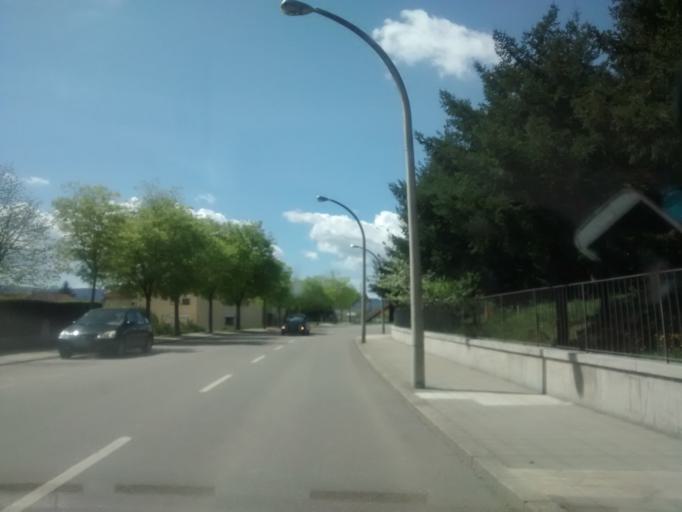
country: PT
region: Braganca
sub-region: Braganca Municipality
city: Braganca
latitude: 41.8027
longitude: -6.7637
